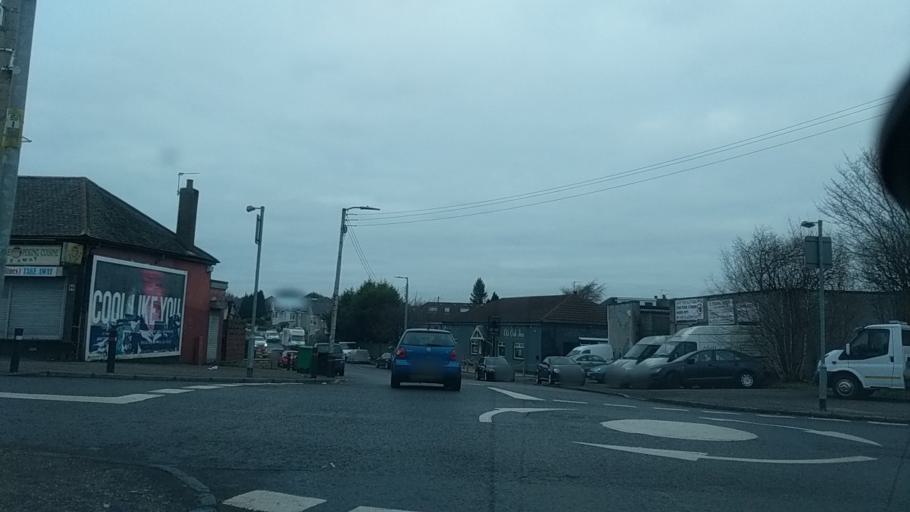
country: GB
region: Scotland
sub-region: South Lanarkshire
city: Rutherglen
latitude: 55.8184
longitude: -4.1907
